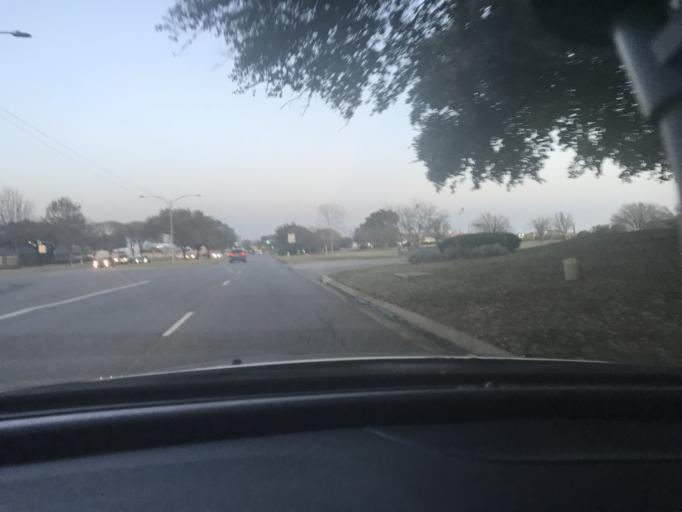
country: US
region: Texas
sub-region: Tarrant County
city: Arlington
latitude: 32.7645
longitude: -97.1011
